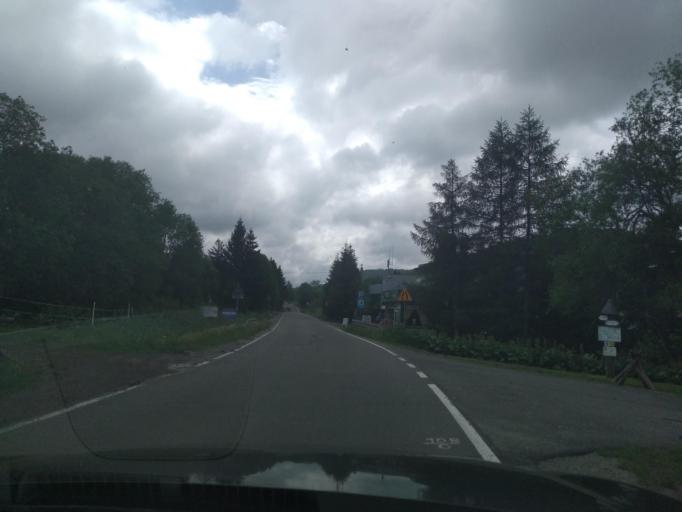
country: PL
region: Subcarpathian Voivodeship
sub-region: Powiat bieszczadzki
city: Lutowiska
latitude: 49.0670
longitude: 22.6798
